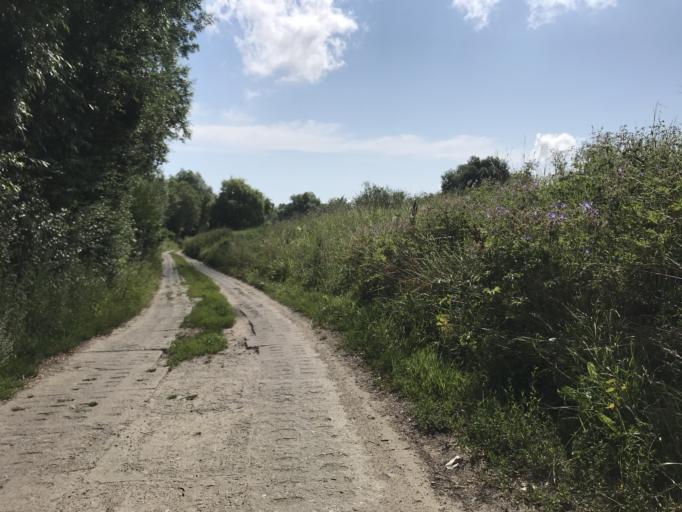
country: PL
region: Pomeranian Voivodeship
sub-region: Gdansk
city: Gdansk
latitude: 54.3252
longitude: 18.6595
